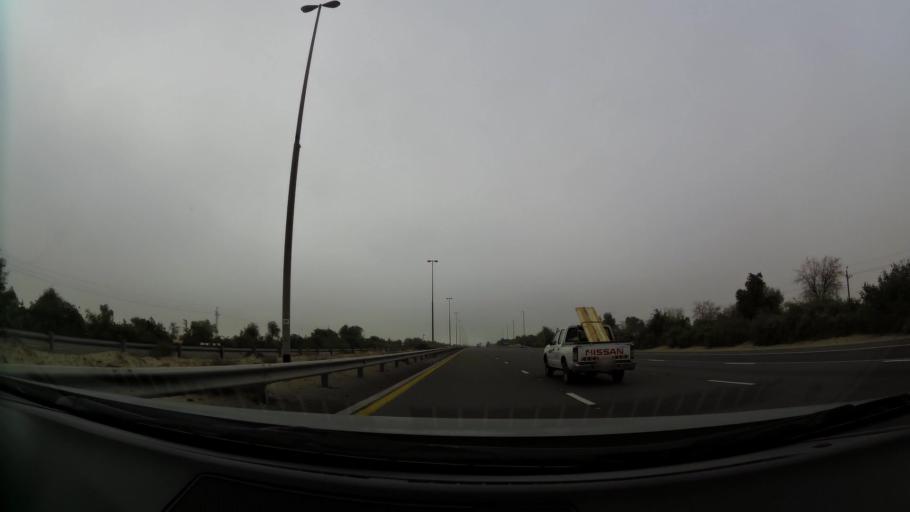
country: AE
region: Dubai
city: Dubai
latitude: 25.0559
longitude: 55.4204
